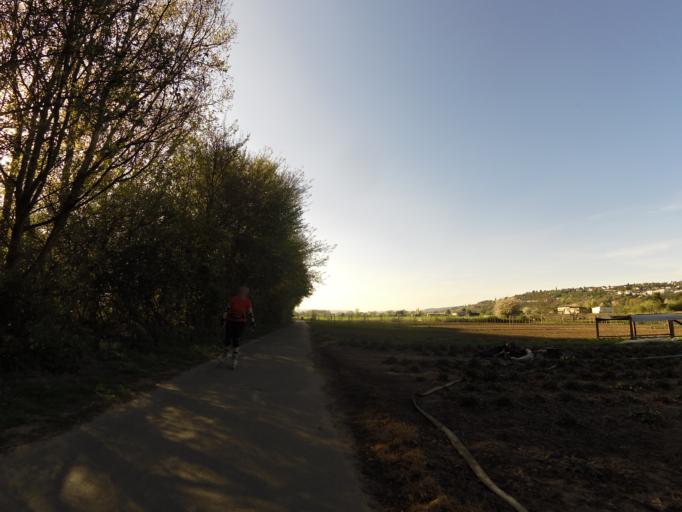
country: DE
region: Rheinland-Pfalz
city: Niederwerth
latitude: 50.3948
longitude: 7.6024
